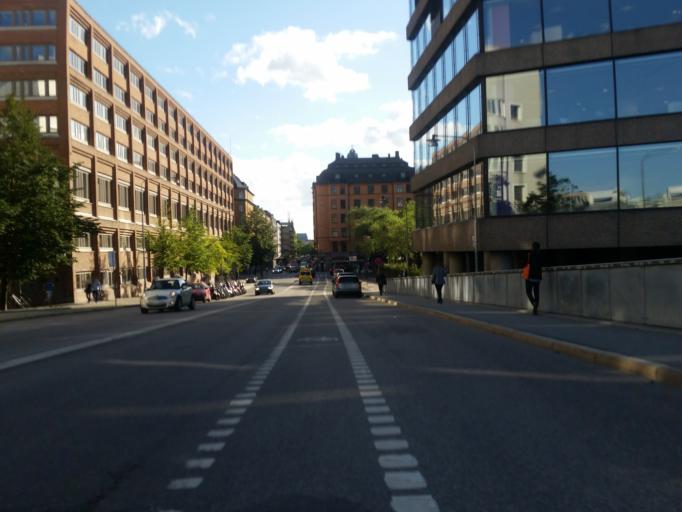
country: SE
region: Stockholm
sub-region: Stockholms Kommun
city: Stockholm
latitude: 59.3344
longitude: 18.0460
